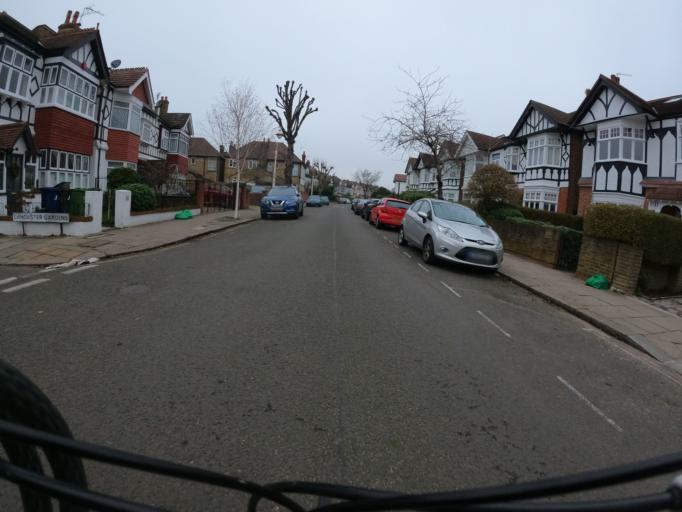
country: GB
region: England
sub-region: Greater London
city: Ealing
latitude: 51.5070
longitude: -0.3160
